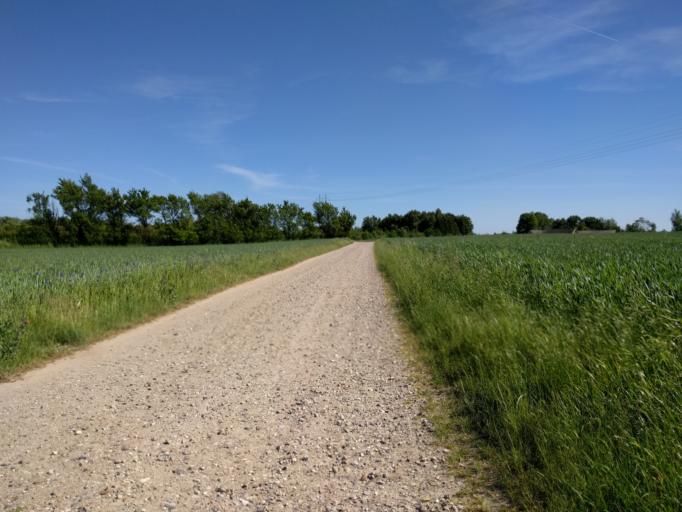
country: DK
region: South Denmark
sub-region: Kerteminde Kommune
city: Langeskov
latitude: 55.3782
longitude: 10.5970
